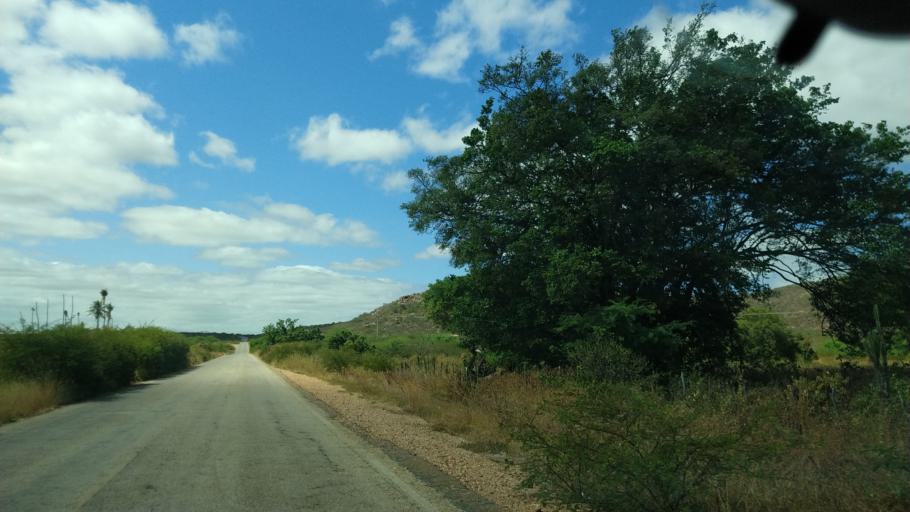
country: BR
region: Rio Grande do Norte
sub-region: Currais Novos
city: Currais Novos
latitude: -6.2641
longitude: -36.5653
